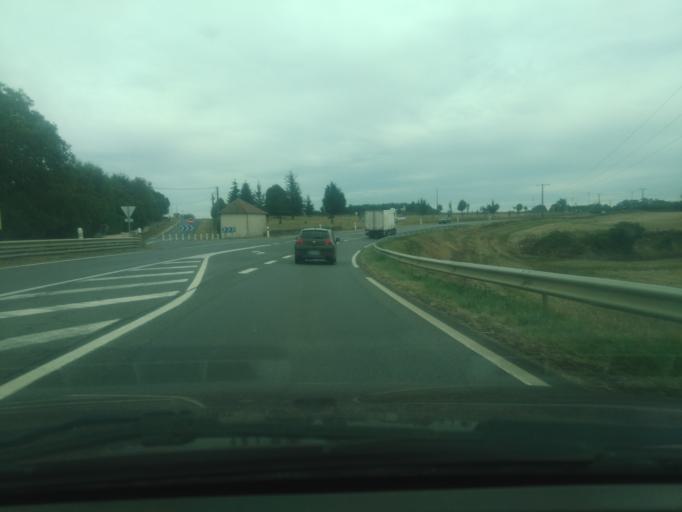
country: FR
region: Poitou-Charentes
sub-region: Departement de la Vienne
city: Saint-Savin
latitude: 46.5678
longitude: 0.8514
